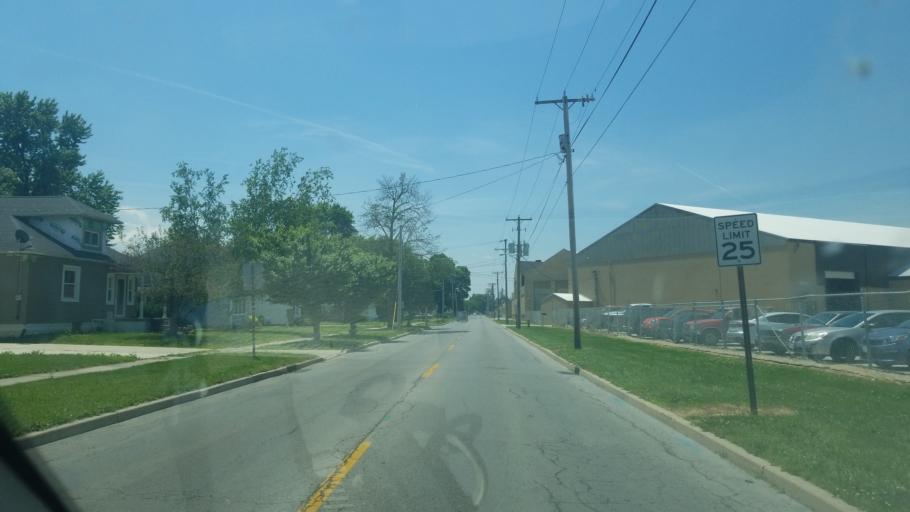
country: US
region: Ohio
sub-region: Hancock County
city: Findlay
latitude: 41.0520
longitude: -83.6428
